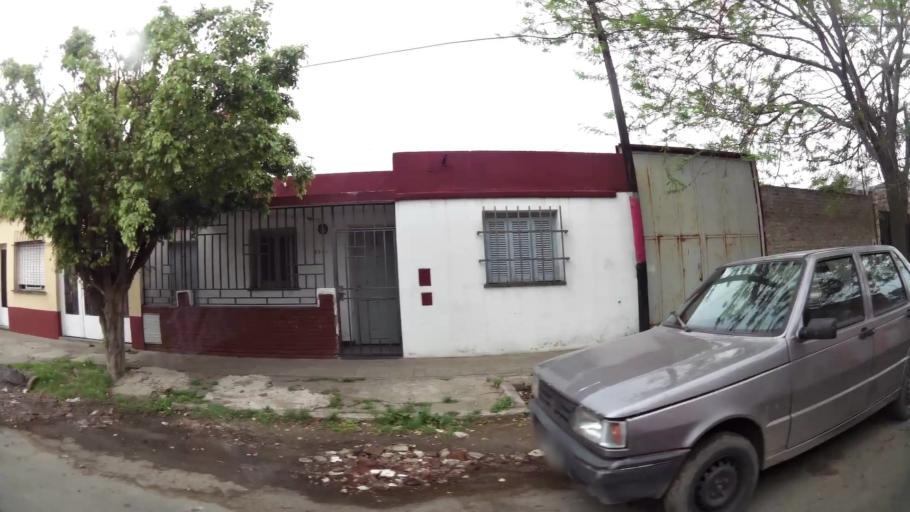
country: AR
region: Santa Fe
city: Gobernador Galvez
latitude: -33.0000
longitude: -60.6621
